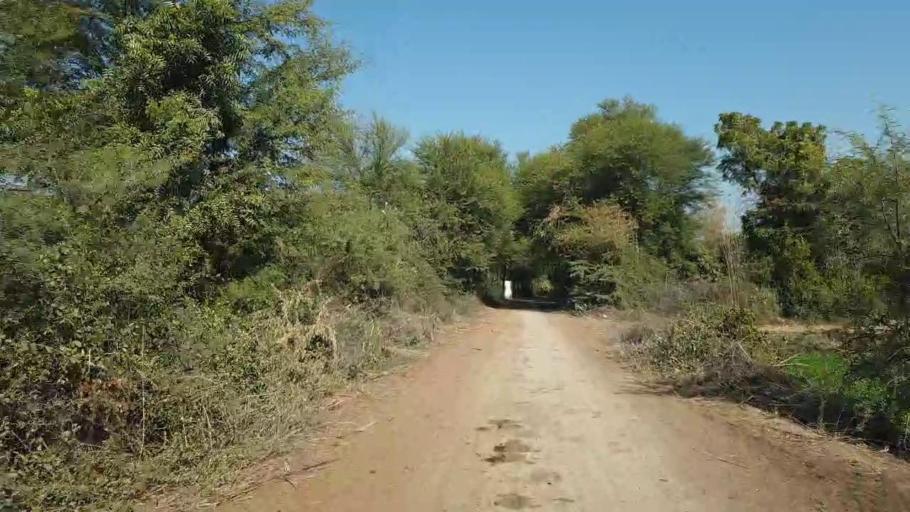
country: PK
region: Sindh
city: Shahpur Chakar
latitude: 26.0620
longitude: 68.4821
